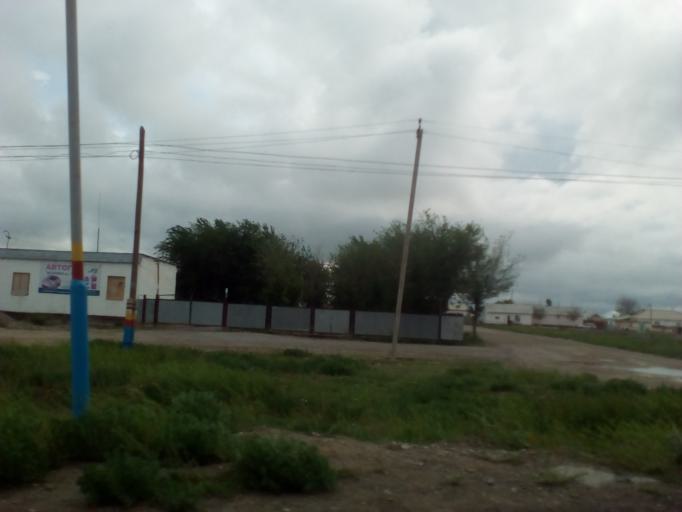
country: KZ
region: Ongtustik Qazaqstan
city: Sholaqqkorghan
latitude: 43.7525
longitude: 69.1941
